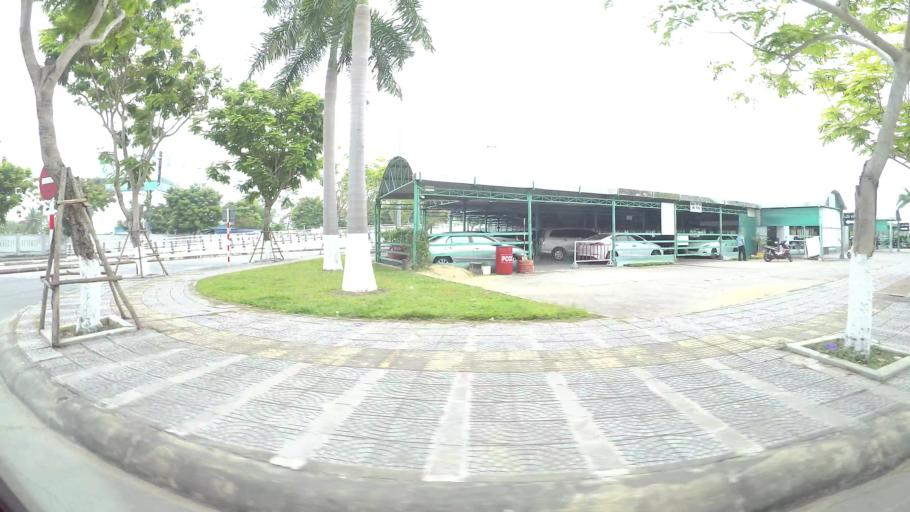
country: VN
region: Da Nang
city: Da Nang
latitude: 16.0509
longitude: 108.2045
